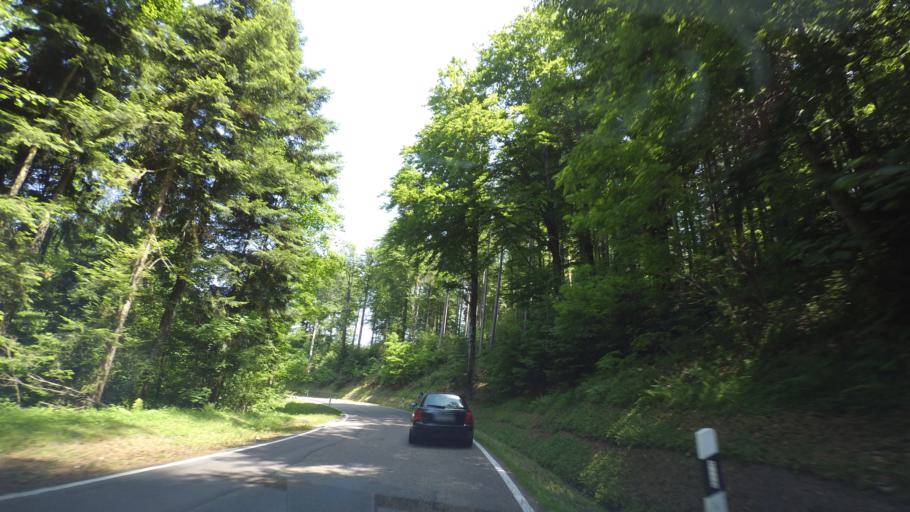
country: DE
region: Baden-Wuerttemberg
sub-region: Regierungsbezirk Stuttgart
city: Kaisersbach
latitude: 48.9452
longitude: 9.6721
